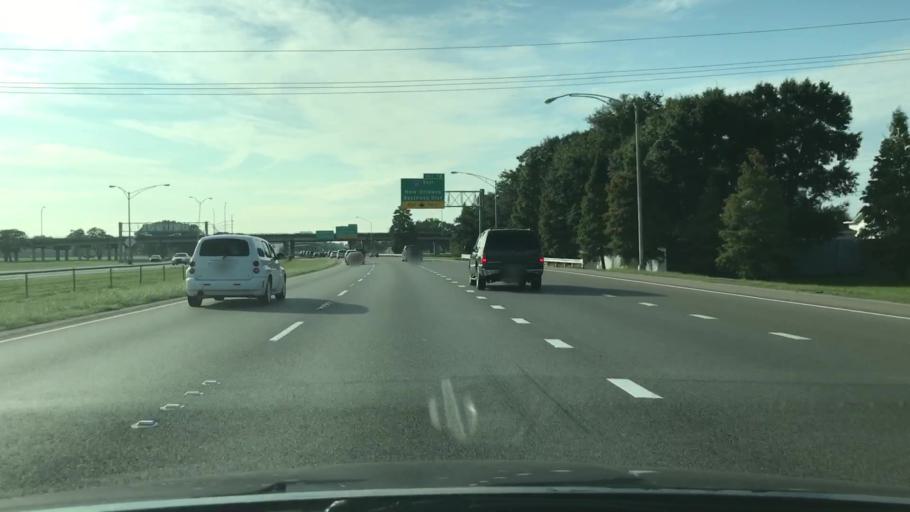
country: US
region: Louisiana
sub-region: Jefferson Parish
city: Metairie
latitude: 29.9948
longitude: -90.1138
